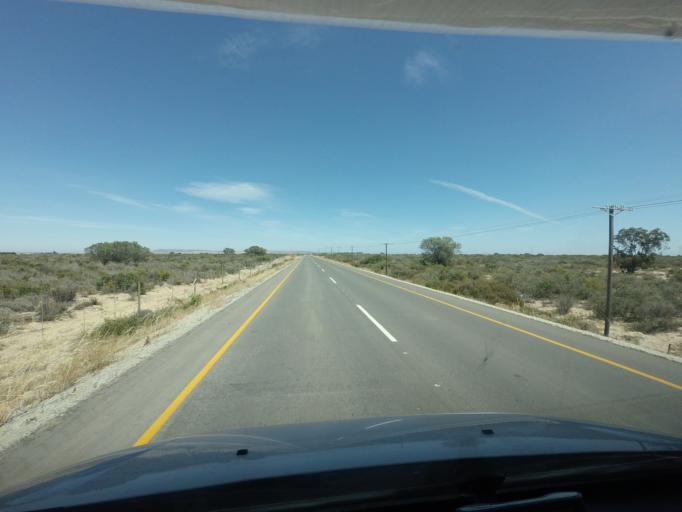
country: ZA
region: Western Cape
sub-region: West Coast District Municipality
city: Vredenburg
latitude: -32.7941
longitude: 18.2384
